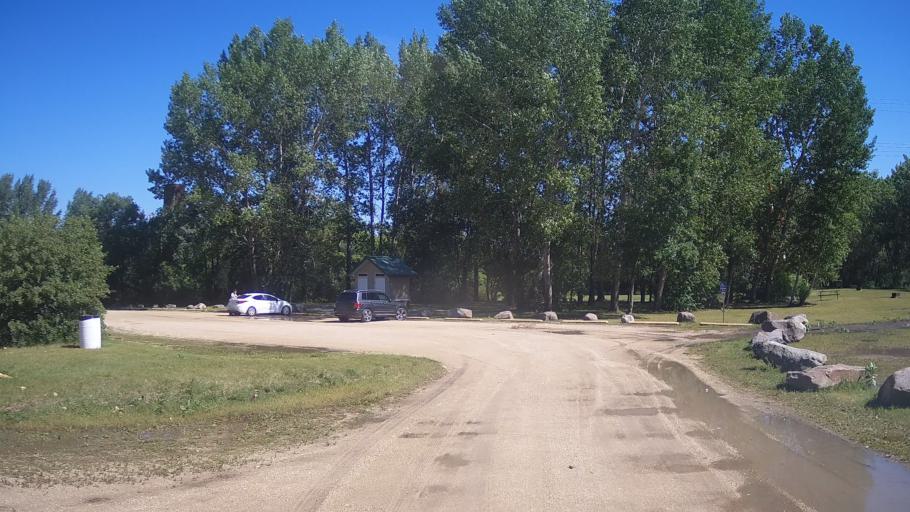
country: CA
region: Manitoba
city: Portage la Prairie
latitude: 49.9473
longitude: -98.3298
